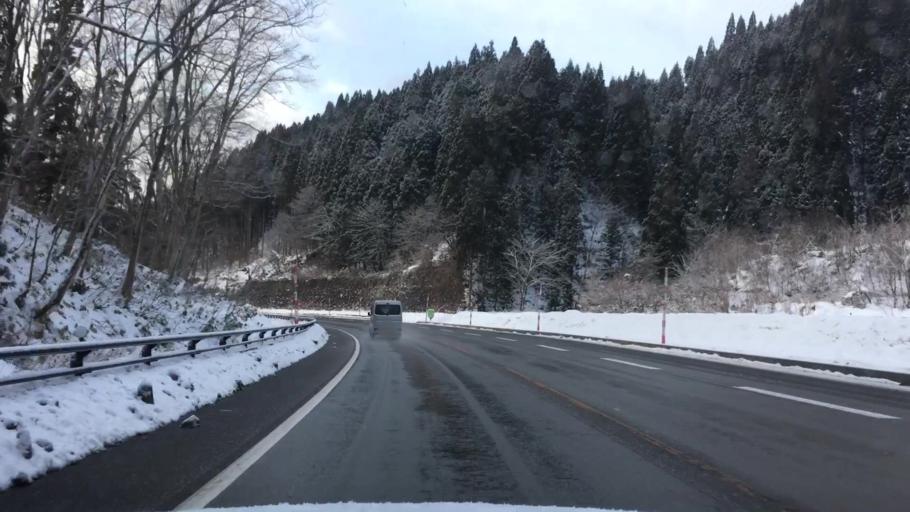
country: JP
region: Akita
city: Odate
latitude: 40.4064
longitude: 140.6085
